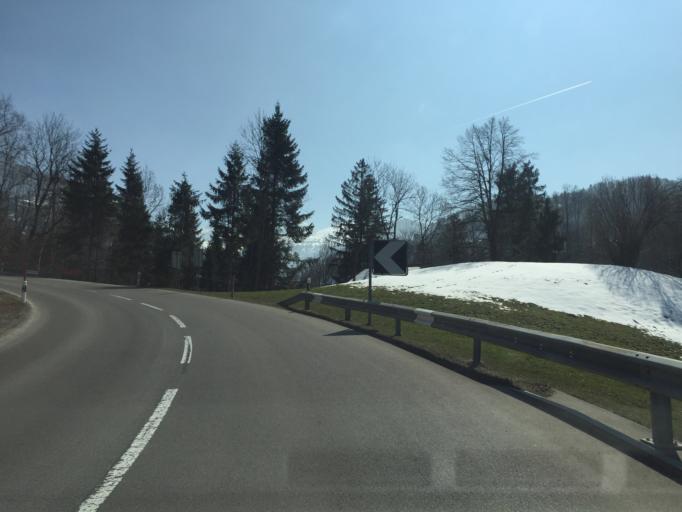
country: CH
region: Saint Gallen
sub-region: Wahlkreis Toggenburg
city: Krummenau
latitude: 47.2198
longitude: 9.2074
